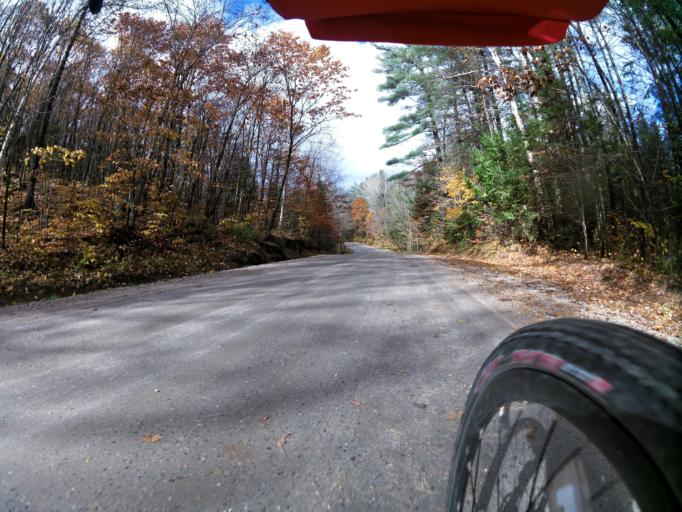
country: CA
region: Quebec
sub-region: Outaouais
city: Wakefield
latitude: 45.7053
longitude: -76.0232
